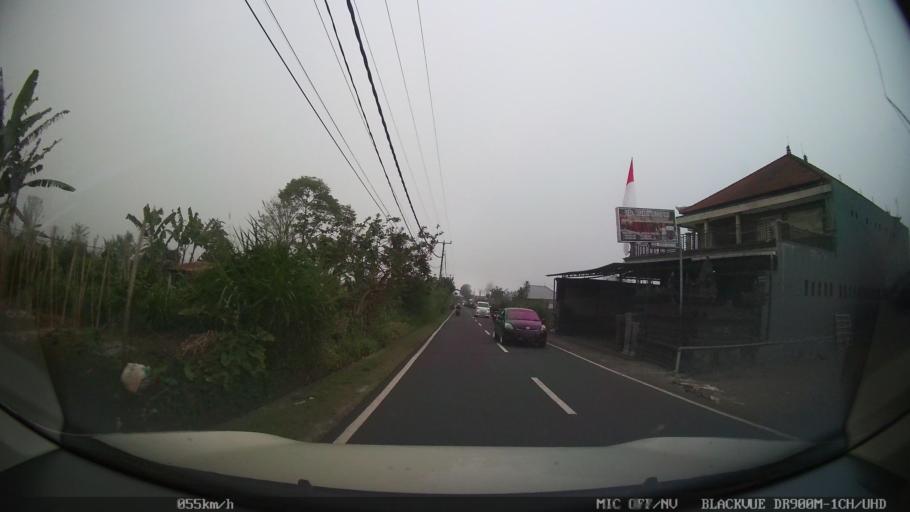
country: ID
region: Bali
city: Banjar Kedisan
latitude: -8.2911
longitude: 115.3173
